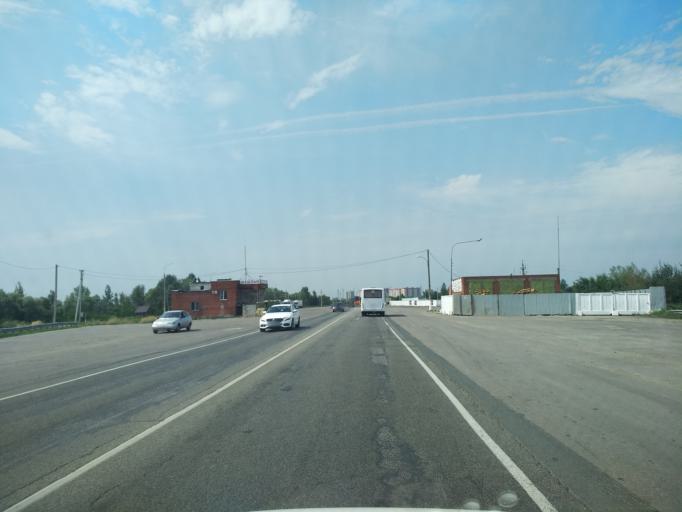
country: RU
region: Voronezj
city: Somovo
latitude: 51.6823
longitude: 39.3455
